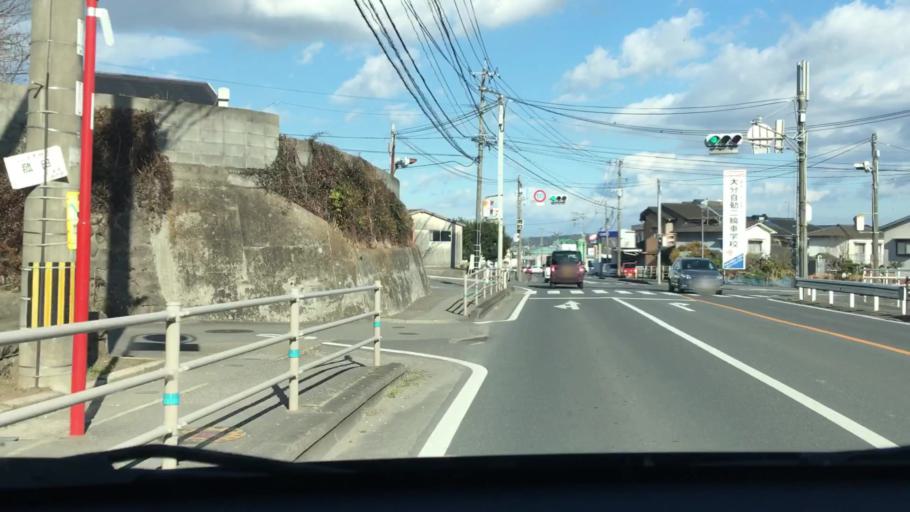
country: JP
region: Oita
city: Tsurusaki
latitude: 33.1771
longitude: 131.6621
